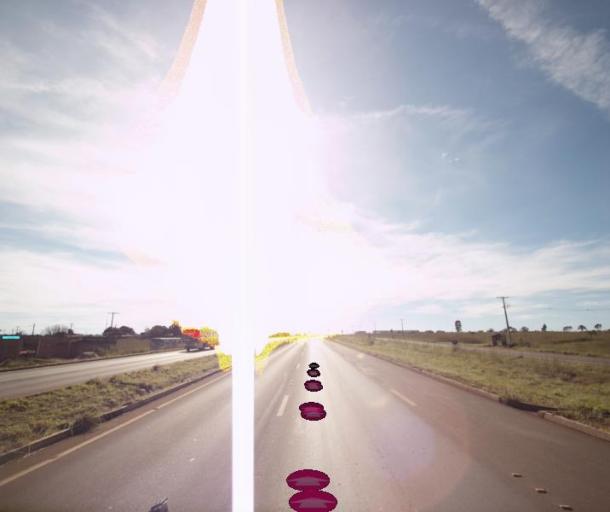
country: BR
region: Federal District
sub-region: Brasilia
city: Brasilia
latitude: -15.7392
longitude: -48.3031
